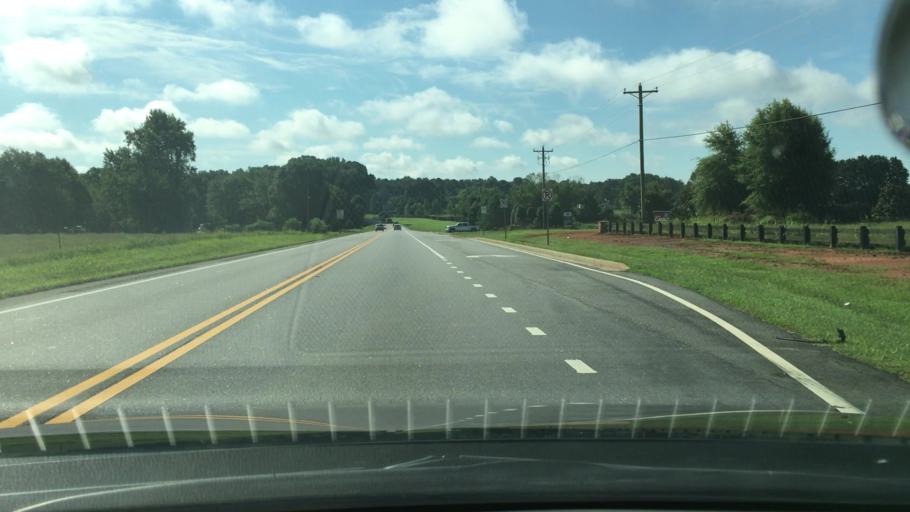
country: US
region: Georgia
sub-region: Morgan County
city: Madison
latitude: 33.5366
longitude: -83.4582
